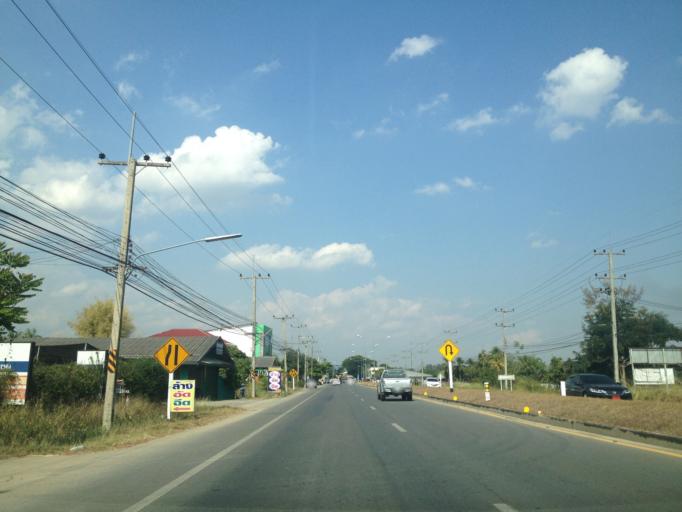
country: TH
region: Chiang Mai
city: San Pa Tong
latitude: 18.5568
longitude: 98.8683
